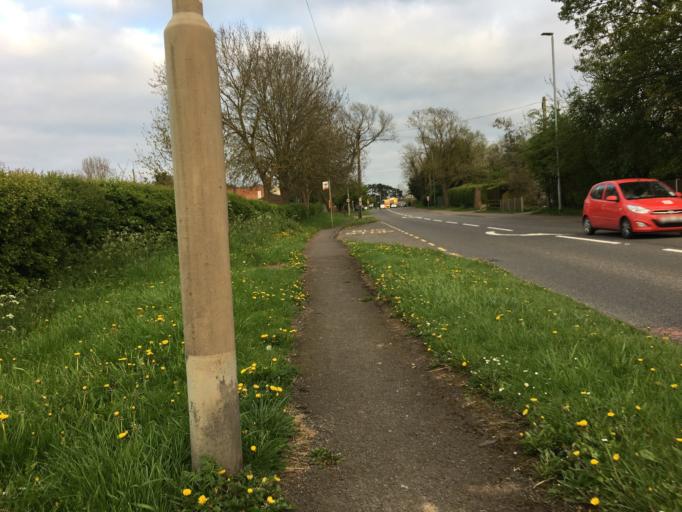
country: GB
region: England
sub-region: Leicestershire
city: Houghton on the Hill
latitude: 52.6284
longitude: -0.9998
